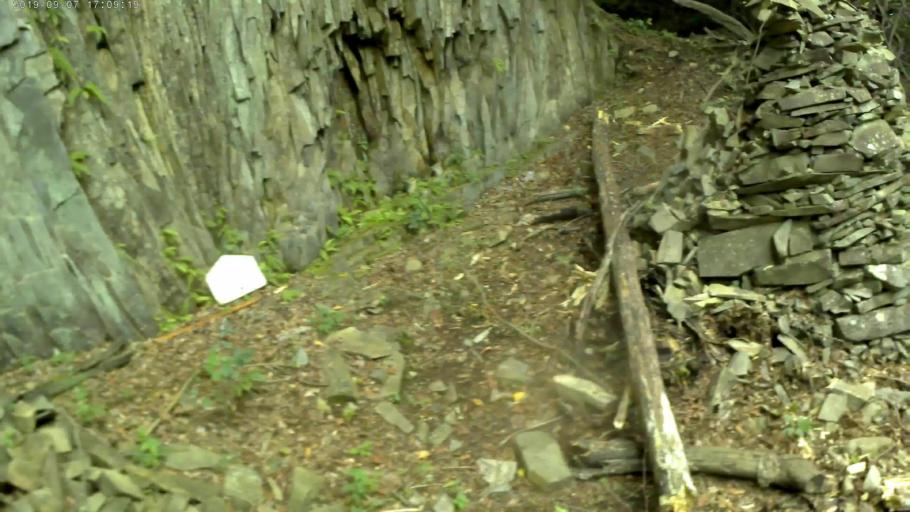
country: JP
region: Gunma
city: Annaka
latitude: 36.3597
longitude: 138.7084
